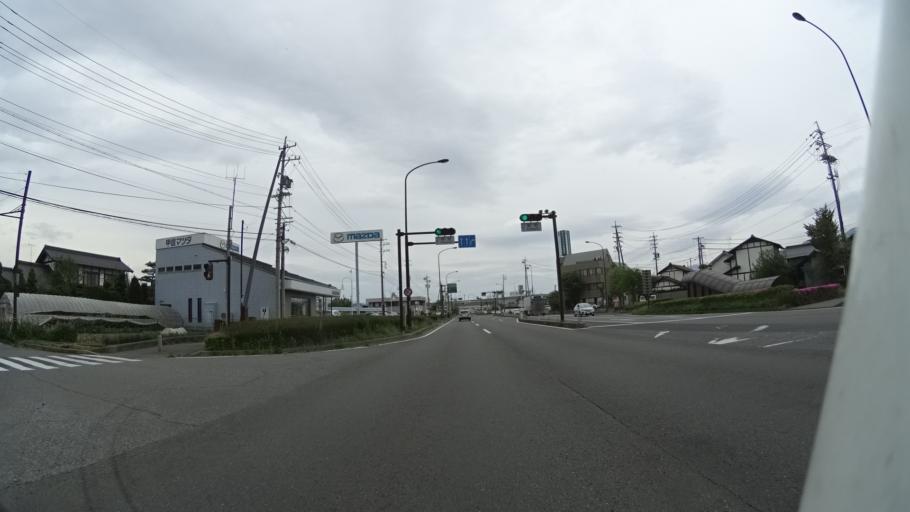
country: JP
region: Nagano
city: Nagano-shi
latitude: 36.5441
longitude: 138.1258
